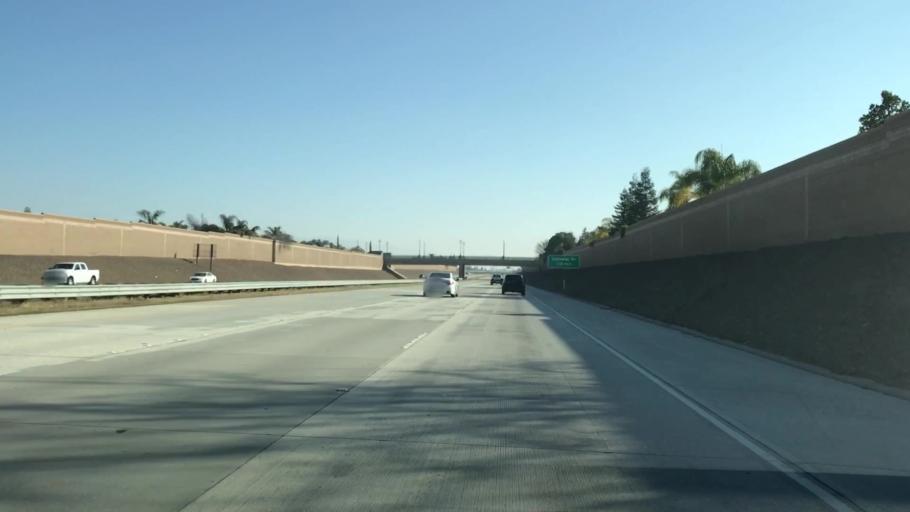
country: US
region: California
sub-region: Kern County
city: Rosedale
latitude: 35.3617
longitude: -119.1318
